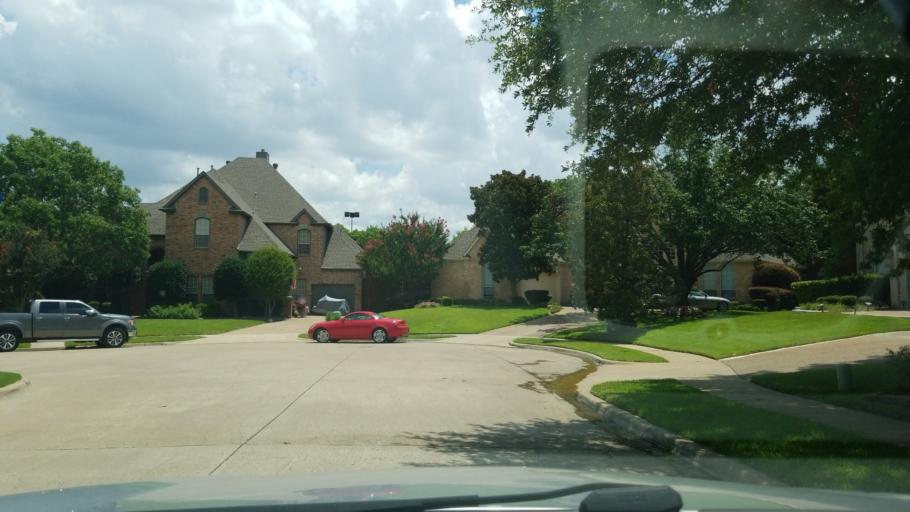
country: US
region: Texas
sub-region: Dallas County
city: Coppell
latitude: 32.9700
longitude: -96.9623
